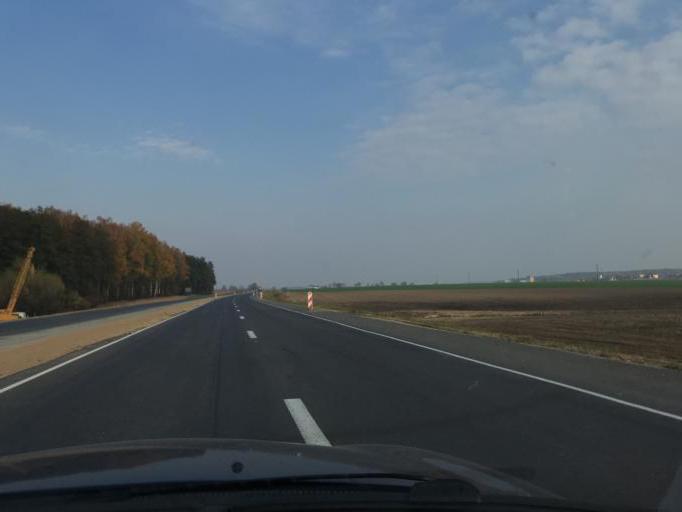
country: BY
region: Grodnenskaya
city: Shchuchin
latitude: 53.7184
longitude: 24.9589
